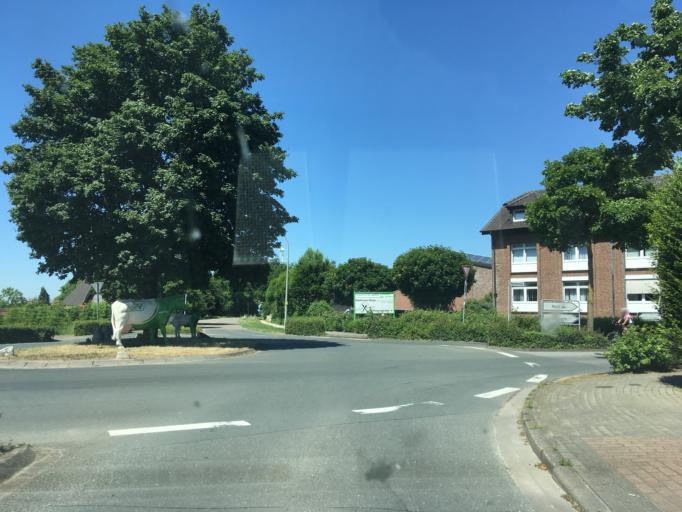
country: DE
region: North Rhine-Westphalia
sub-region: Regierungsbezirk Munster
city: Raesfeld
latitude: 51.7742
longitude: 6.8328
